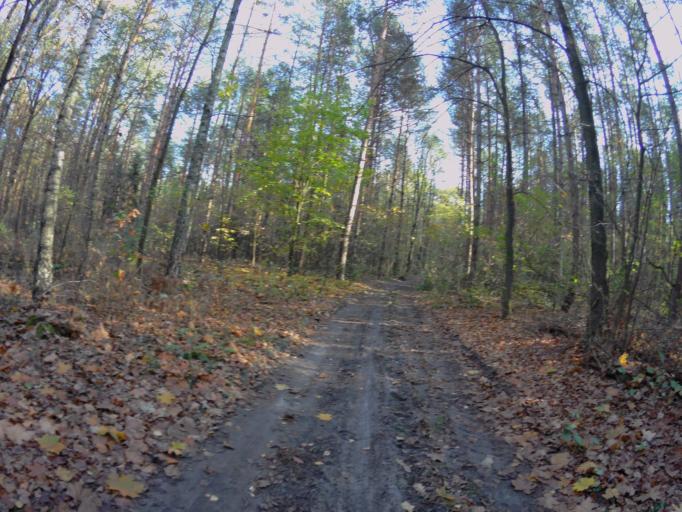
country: PL
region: Subcarpathian Voivodeship
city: Nowa Sarzyna
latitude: 50.3096
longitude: 22.3499
